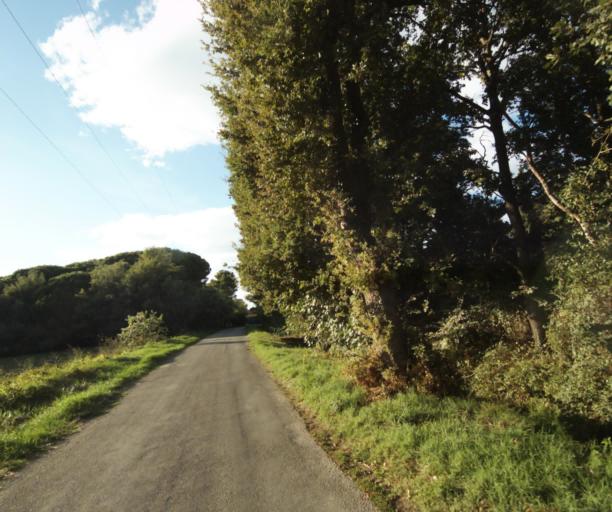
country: FR
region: Languedoc-Roussillon
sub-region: Departement des Pyrenees-Orientales
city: Argelers
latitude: 42.5642
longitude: 3.0134
